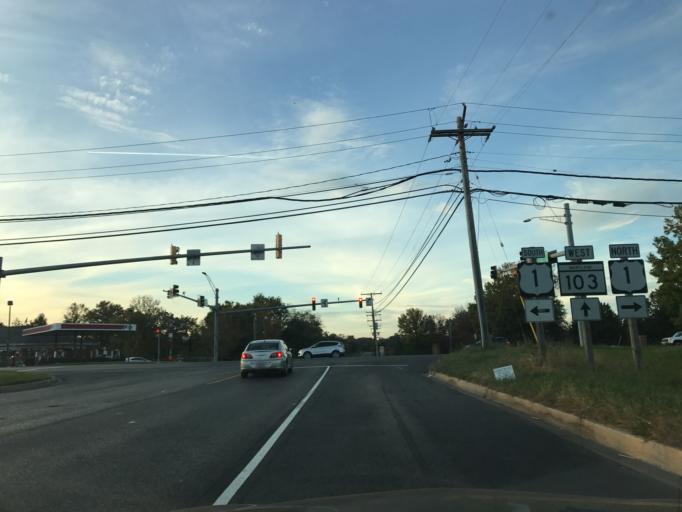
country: US
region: Maryland
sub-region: Anne Arundel County
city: Jessup
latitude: 39.1837
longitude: -76.7633
